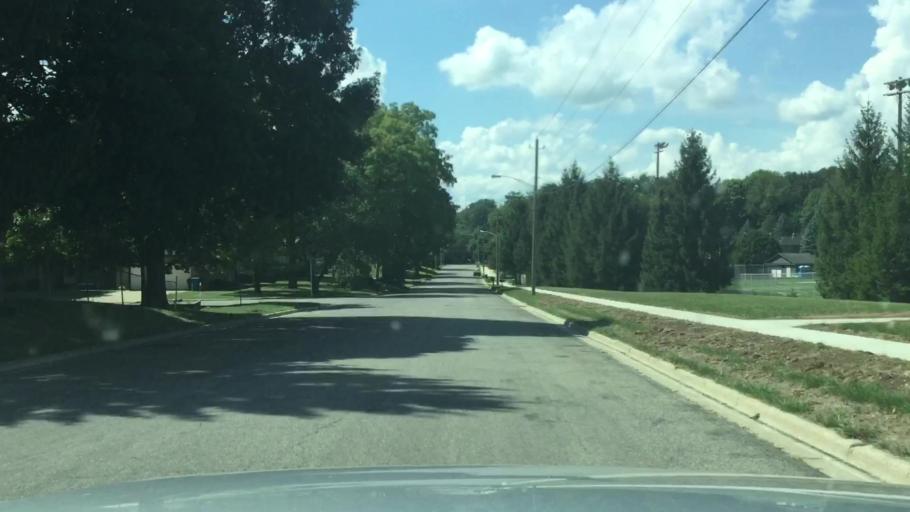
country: US
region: Michigan
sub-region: Lenawee County
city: Clinton
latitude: 42.0722
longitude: -83.9636
